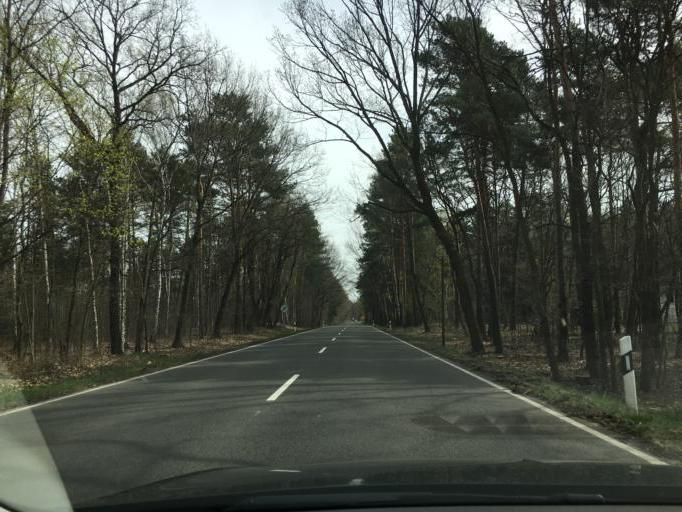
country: DE
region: Saxony
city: Gross Duben
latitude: 51.5816
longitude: 14.5637
